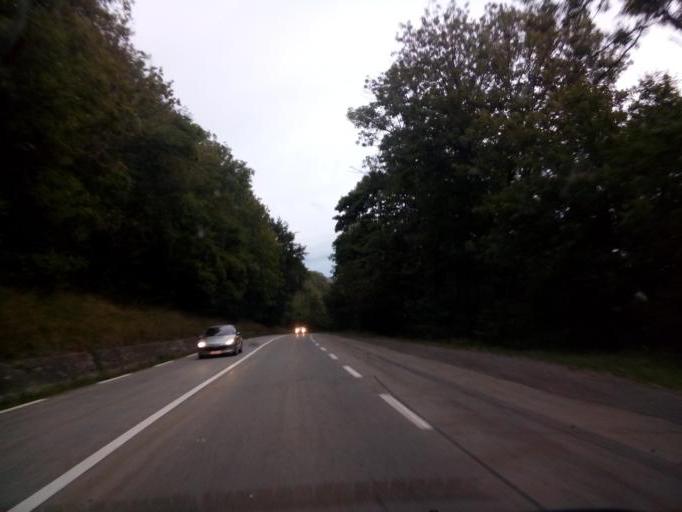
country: FR
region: Rhone-Alpes
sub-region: Departement de l'Isere
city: Pierre-Chatel
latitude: 45.0088
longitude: 5.7730
